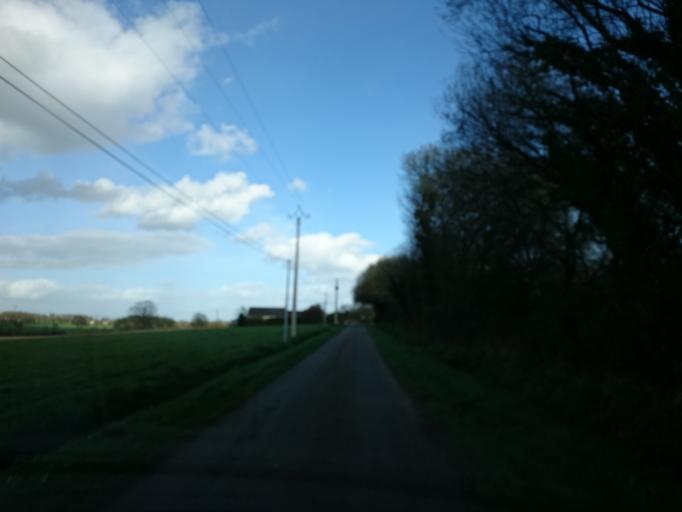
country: FR
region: Brittany
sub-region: Departement d'Ille-et-Vilaine
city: Crevin
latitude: 47.9220
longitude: -1.6475
